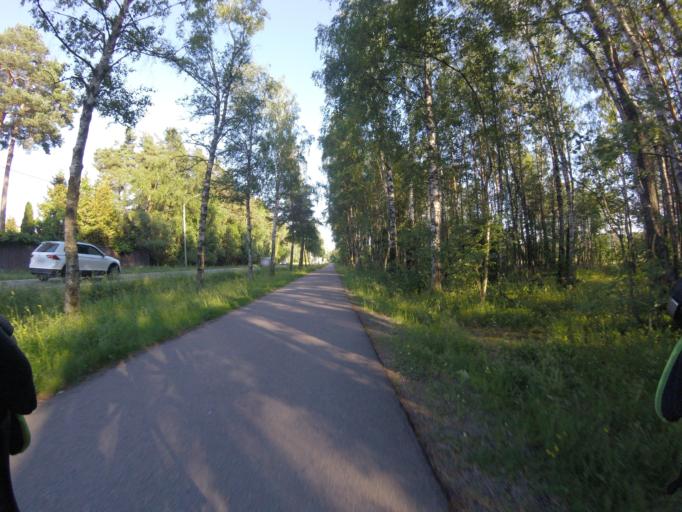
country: NO
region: Akershus
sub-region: Skedsmo
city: Lillestrom
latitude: 59.9657
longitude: 11.0553
